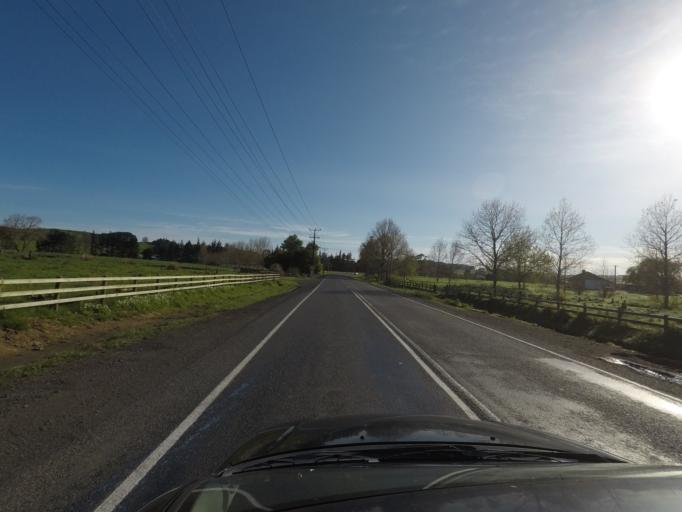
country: NZ
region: Auckland
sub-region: Auckland
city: Red Hill
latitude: -37.0044
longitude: 174.9561
